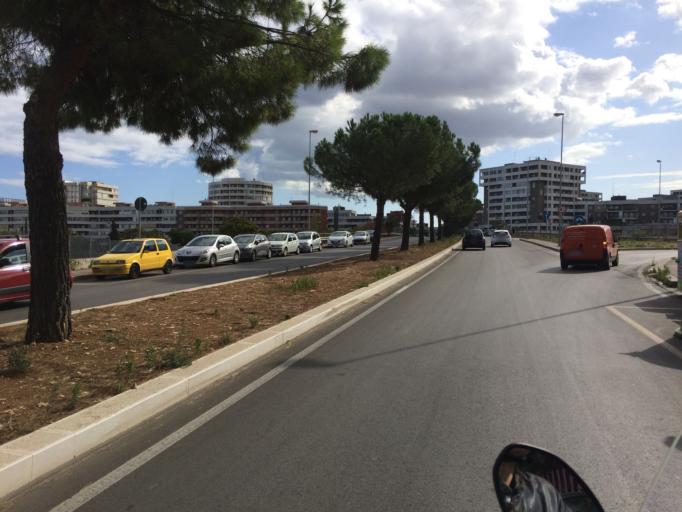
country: IT
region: Apulia
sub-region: Provincia di Bari
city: Bari
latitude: 41.0933
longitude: 16.8561
